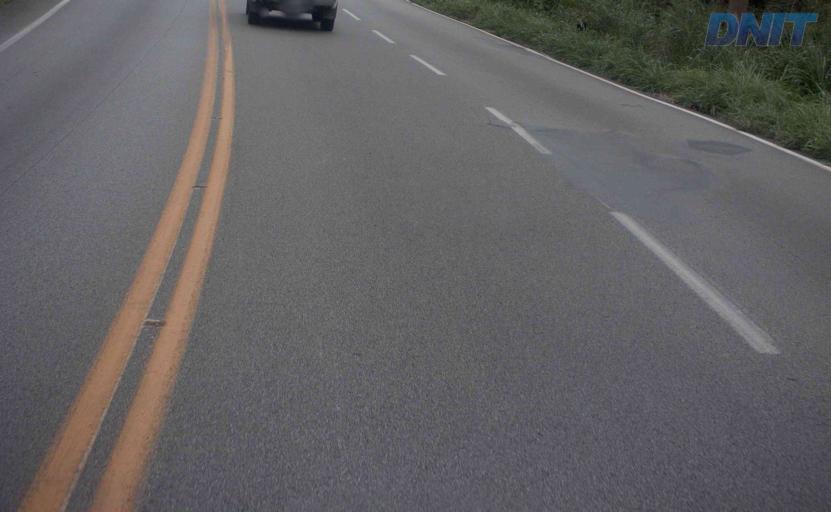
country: BR
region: Minas Gerais
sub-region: Joao Monlevade
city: Joao Monlevade
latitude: -19.8422
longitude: -43.1004
